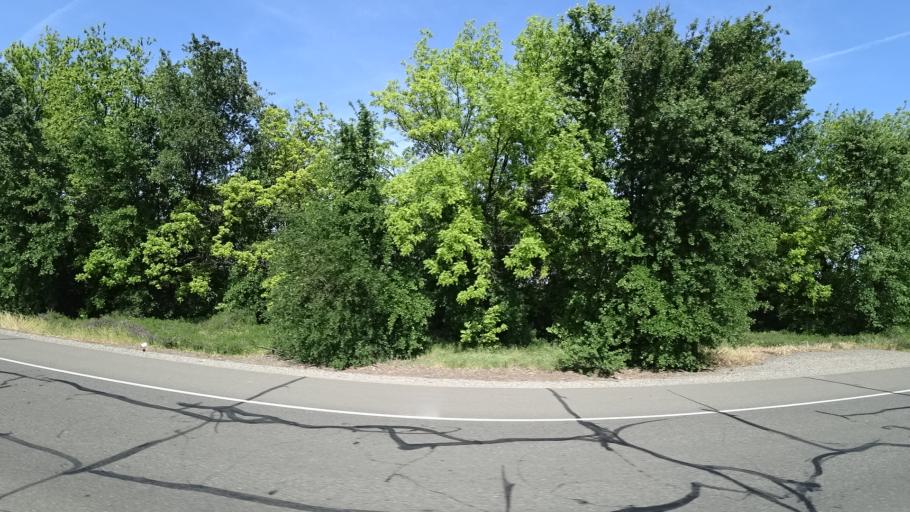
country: US
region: California
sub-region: Tehama County
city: Los Molinos
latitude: 40.0091
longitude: -122.0939
